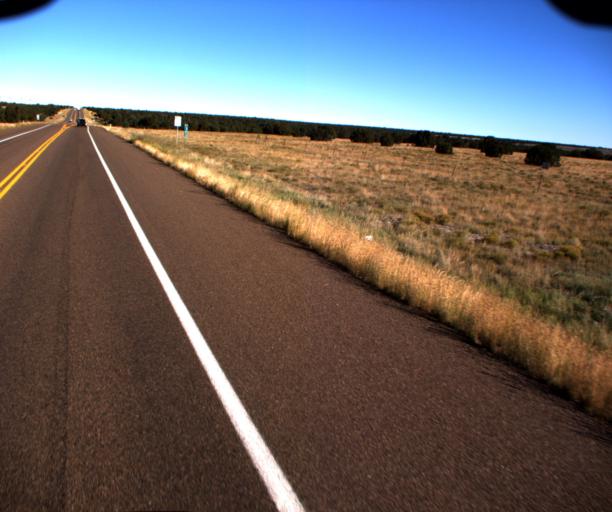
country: US
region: Arizona
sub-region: Navajo County
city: Show Low
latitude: 34.2673
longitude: -110.0220
